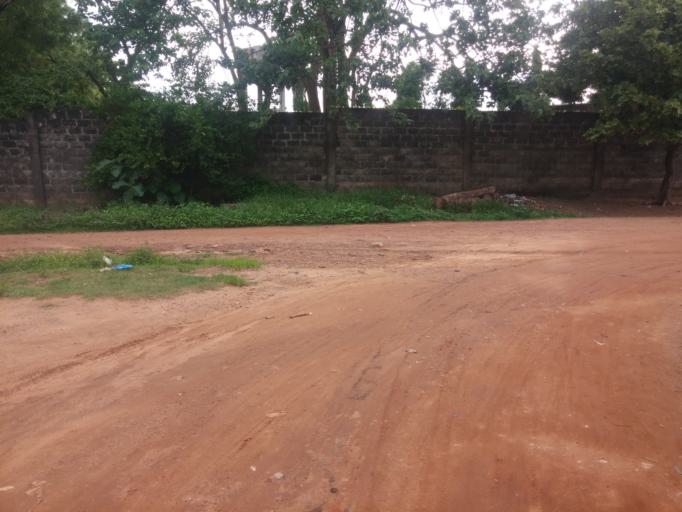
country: TG
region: Kara
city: Kara
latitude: 9.5453
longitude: 1.2031
